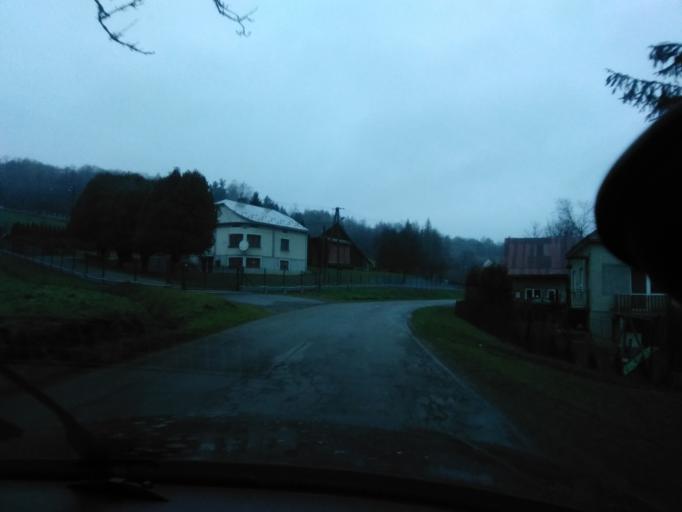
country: PL
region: Subcarpathian Voivodeship
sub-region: Powiat brzozowski
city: Nozdrzec
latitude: 49.7538
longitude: 22.1447
